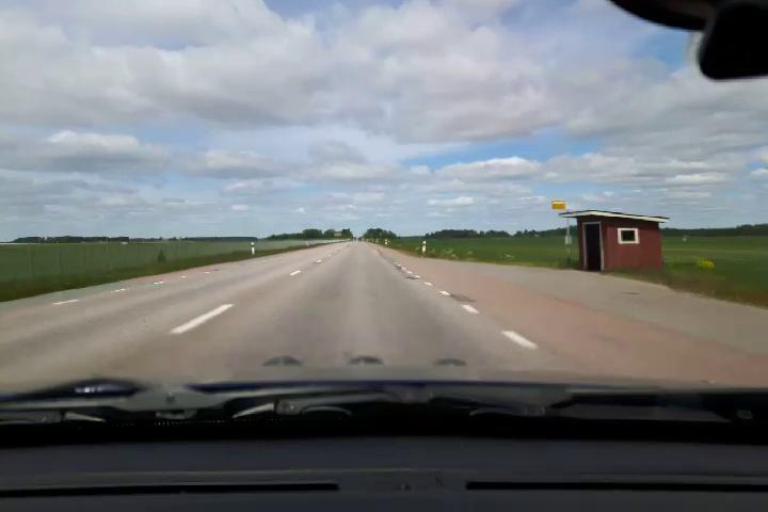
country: SE
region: Uppsala
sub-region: Uppsala Kommun
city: Gamla Uppsala
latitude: 59.8937
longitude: 17.6155
